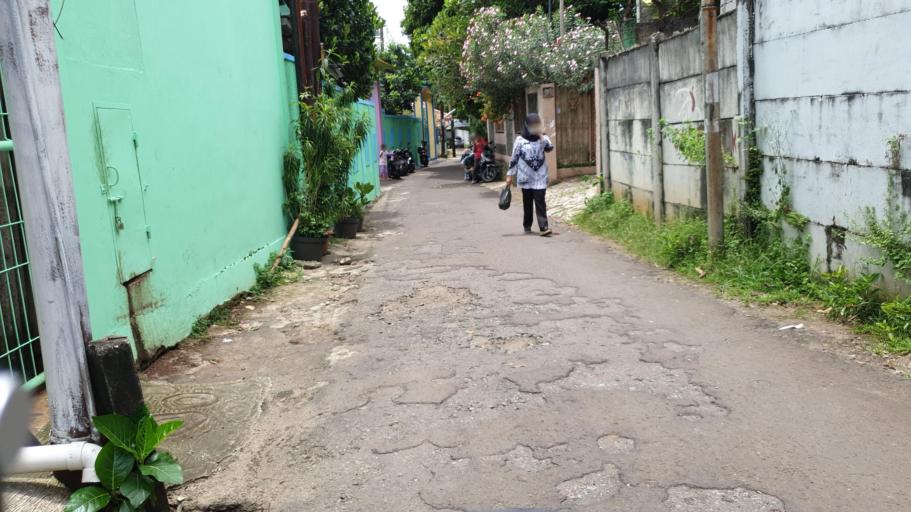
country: ID
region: West Java
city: Pamulang
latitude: -6.3041
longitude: 106.7837
